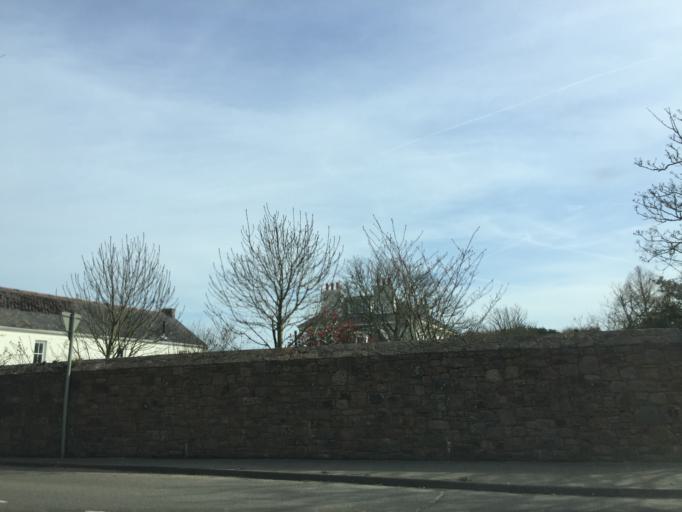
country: JE
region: St Helier
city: Saint Helier
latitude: 49.2206
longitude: -2.0579
